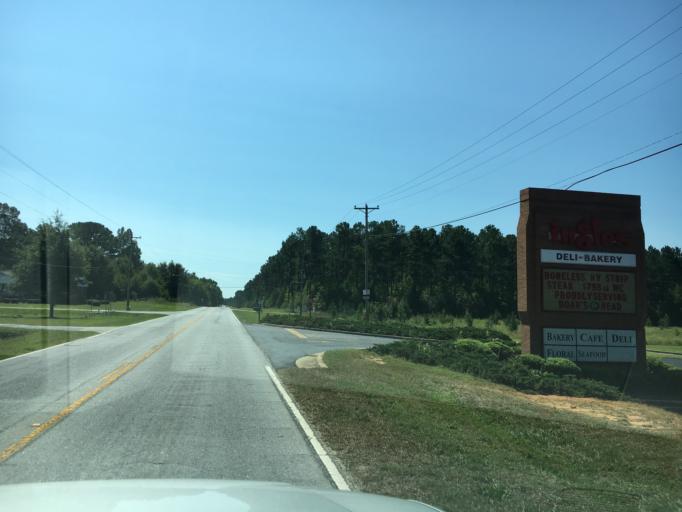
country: US
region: South Carolina
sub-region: Laurens County
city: Clinton
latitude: 34.4485
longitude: -81.8735
